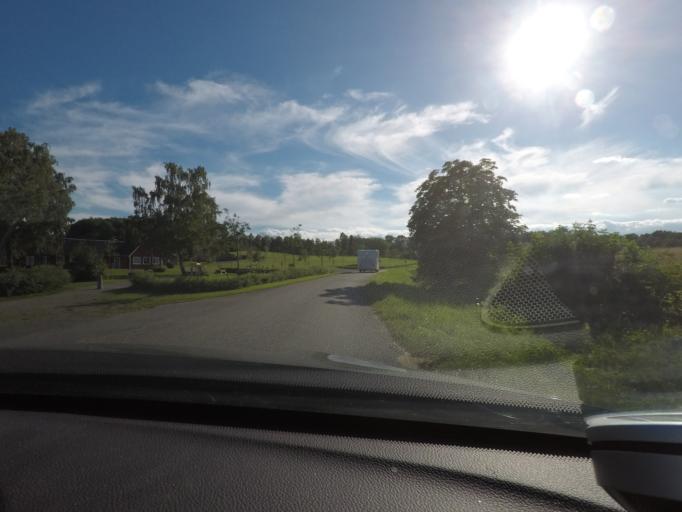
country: SE
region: Skane
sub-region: Hassleholms Kommun
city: Hassleholm
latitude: 56.1192
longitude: 13.8263
